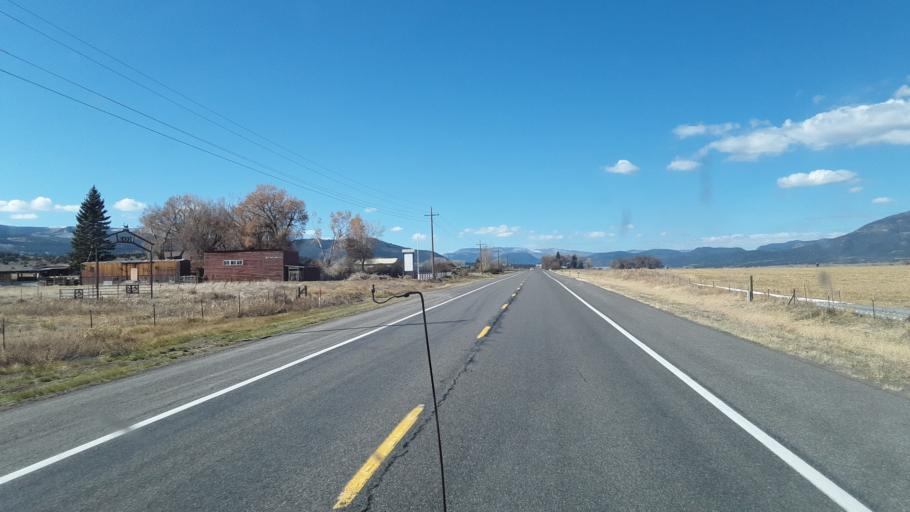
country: US
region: Colorado
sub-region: Rio Grande County
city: Del Norte
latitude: 37.6769
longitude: -106.4683
